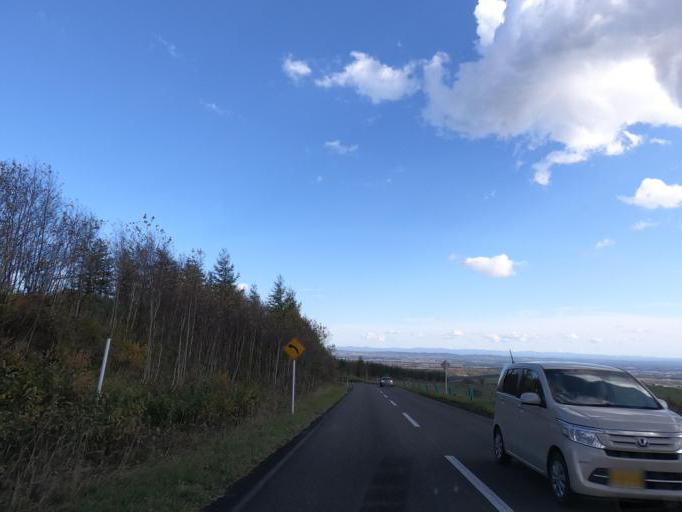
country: JP
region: Hokkaido
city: Otofuke
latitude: 43.2903
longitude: 143.2085
